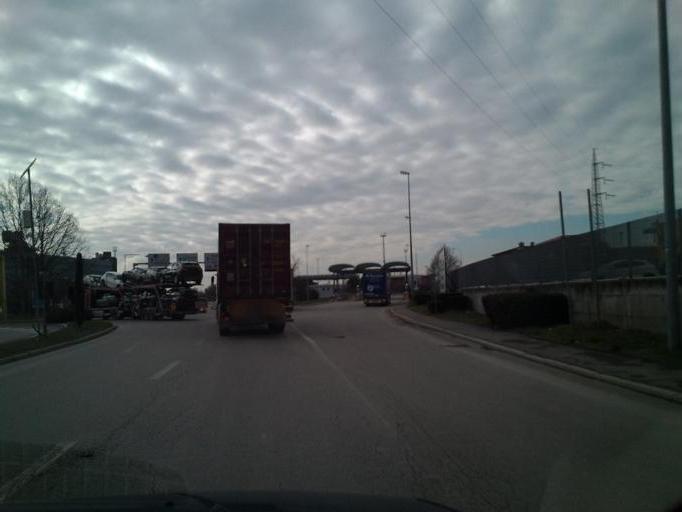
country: IT
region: Veneto
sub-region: Provincia di Verona
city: Dossobuono
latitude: 45.4186
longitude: 10.9299
